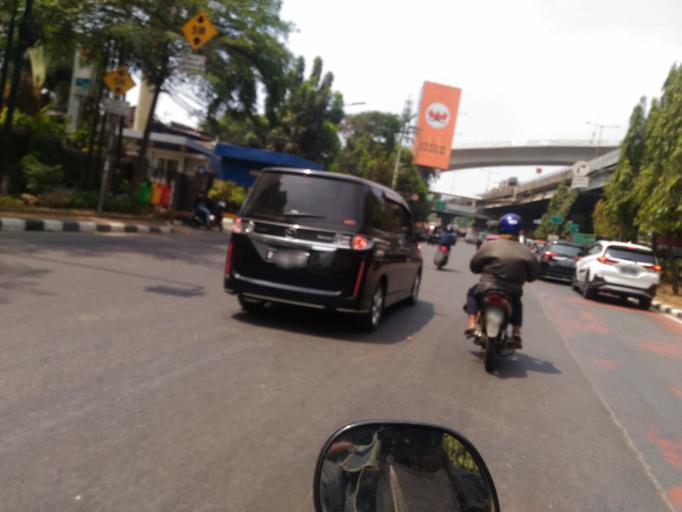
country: ID
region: Jakarta Raya
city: Jakarta
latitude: -6.2404
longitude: 106.8775
